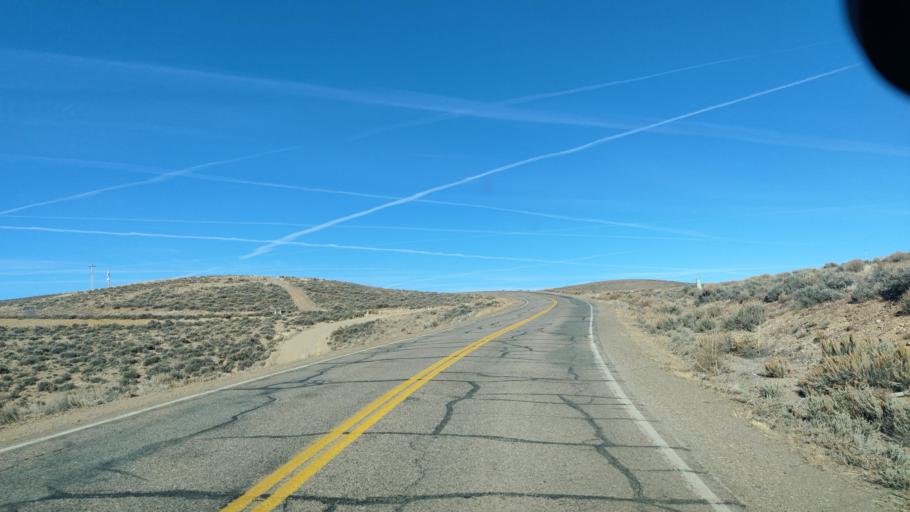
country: US
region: Colorado
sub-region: Gunnison County
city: Gunnison
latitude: 38.5343
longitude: -106.9581
